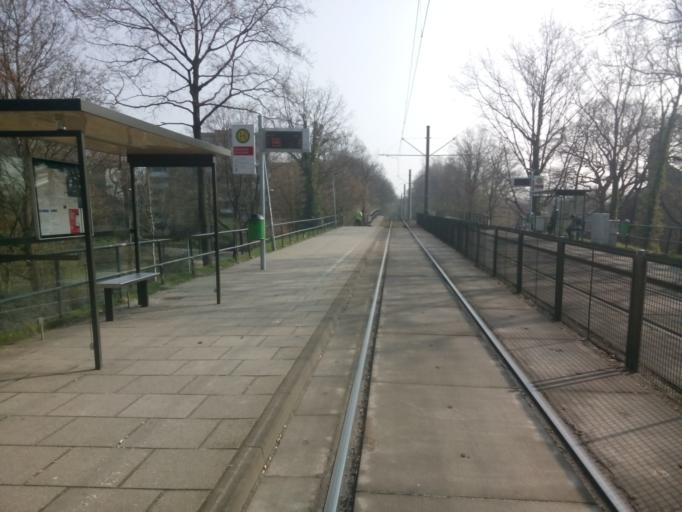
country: DE
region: Lower Saxony
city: Lilienthal
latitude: 53.0745
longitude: 8.9369
